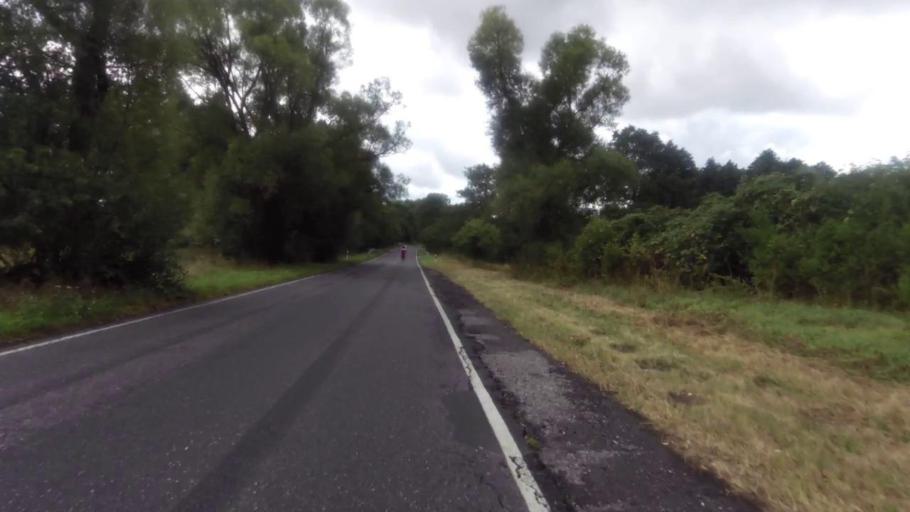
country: PL
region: West Pomeranian Voivodeship
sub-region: Powiat mysliborski
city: Debno
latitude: 52.6898
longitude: 14.6461
